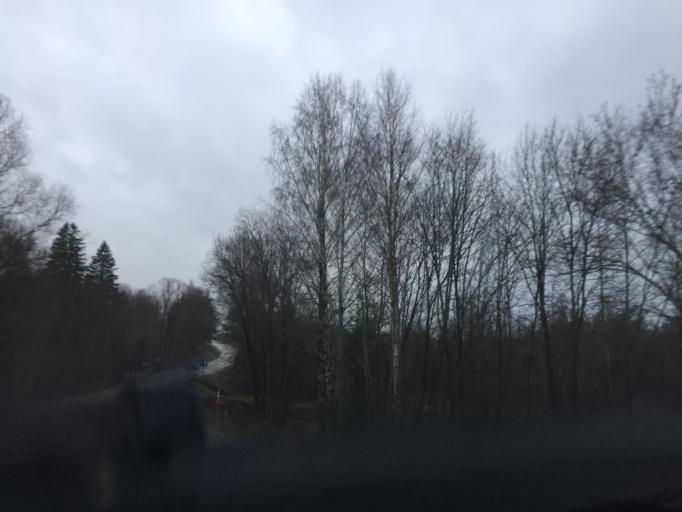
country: LV
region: Salacgrivas
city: Salacgriva
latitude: 57.7597
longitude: 24.4549
